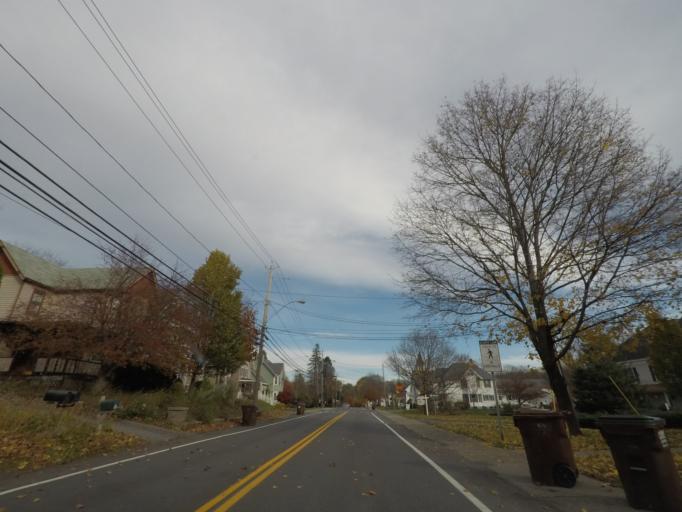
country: US
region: New York
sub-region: Albany County
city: Voorheesville
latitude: 42.6498
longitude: -73.9314
